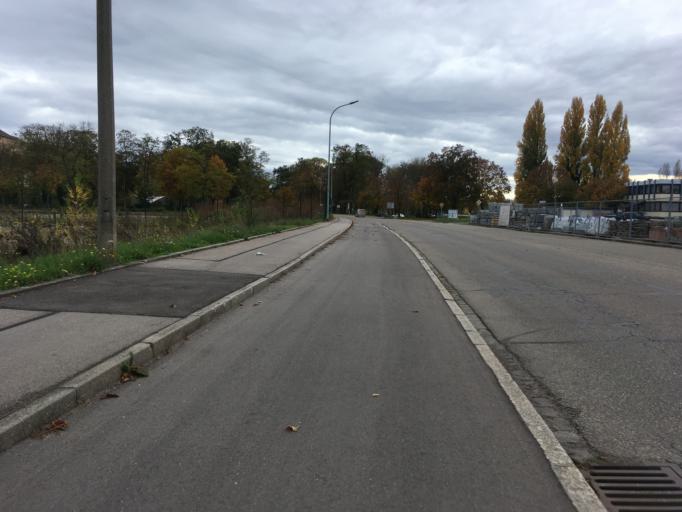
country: DE
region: Baden-Wuerttemberg
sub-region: Freiburg Region
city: Breisach am Rhein
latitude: 48.0334
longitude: 7.5722
